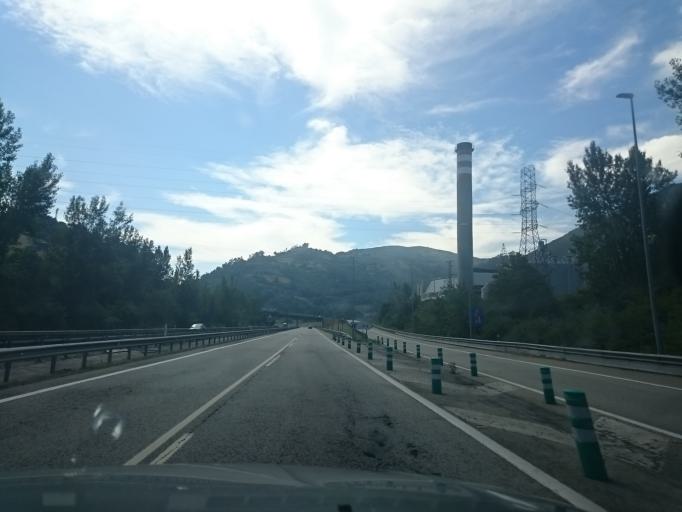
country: ES
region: Asturias
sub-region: Province of Asturias
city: Mieres
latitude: 43.2751
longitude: -5.8088
